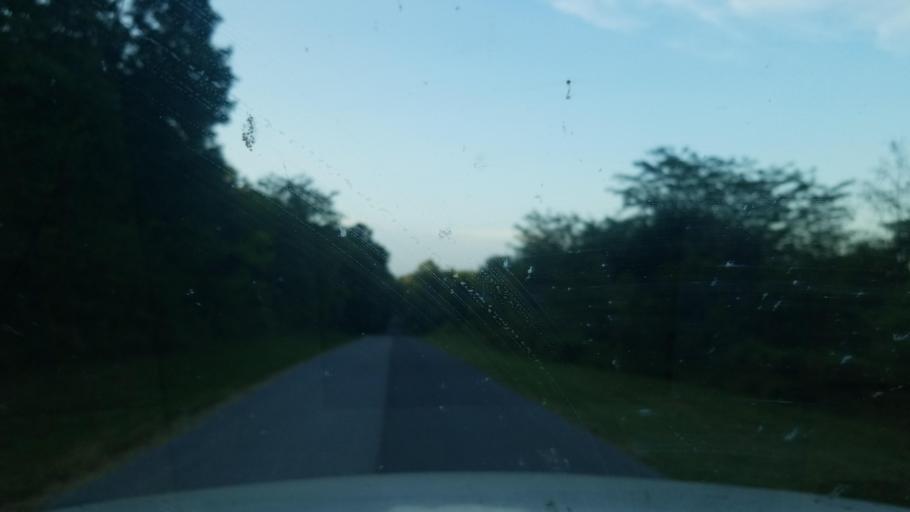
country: US
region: Illinois
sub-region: Saline County
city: Carrier Mills
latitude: 37.7796
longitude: -88.7122
